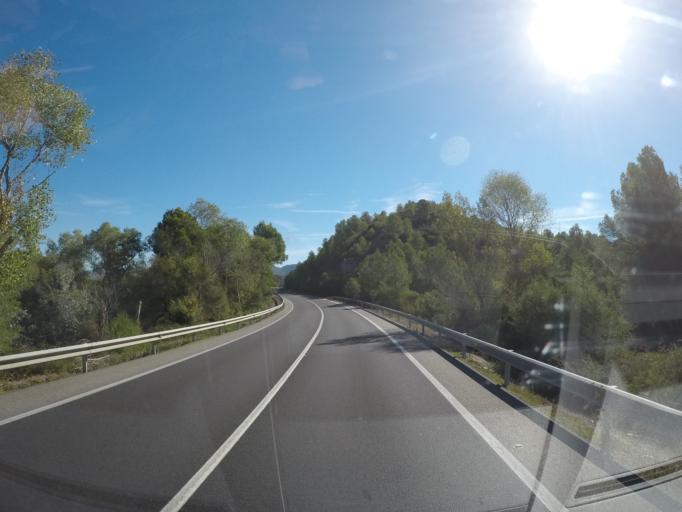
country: ES
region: Catalonia
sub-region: Provincia de Tarragona
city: Miravet
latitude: 41.0320
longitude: 0.6124
